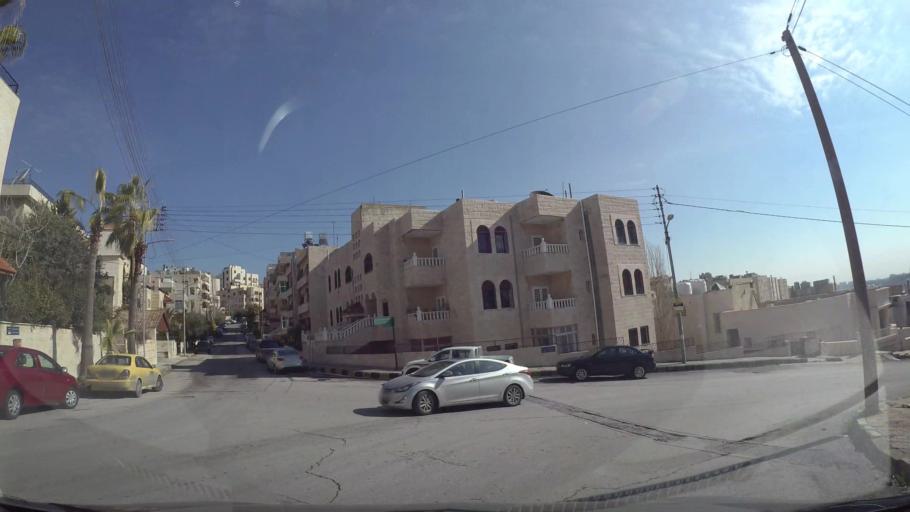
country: JO
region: Amman
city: Al Jubayhah
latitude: 32.0043
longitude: 35.8856
